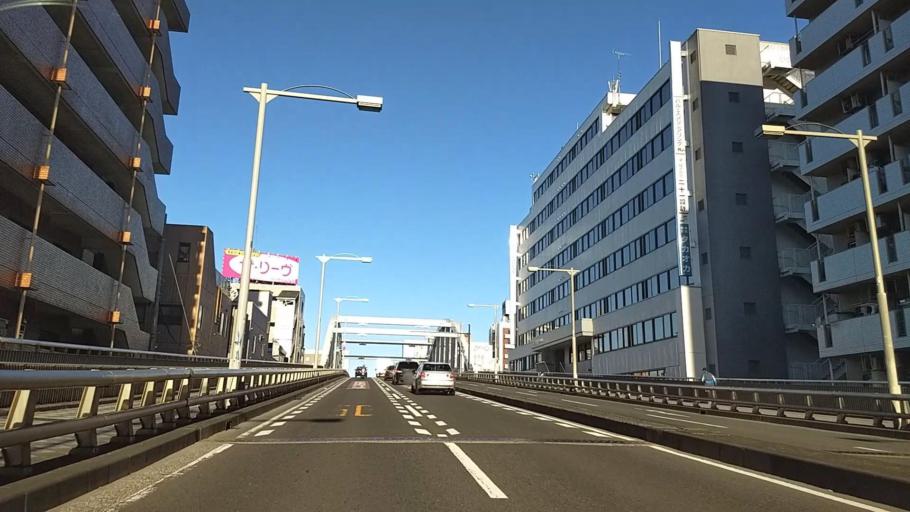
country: JP
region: Kanagawa
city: Yokohama
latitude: 35.4612
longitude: 139.6195
